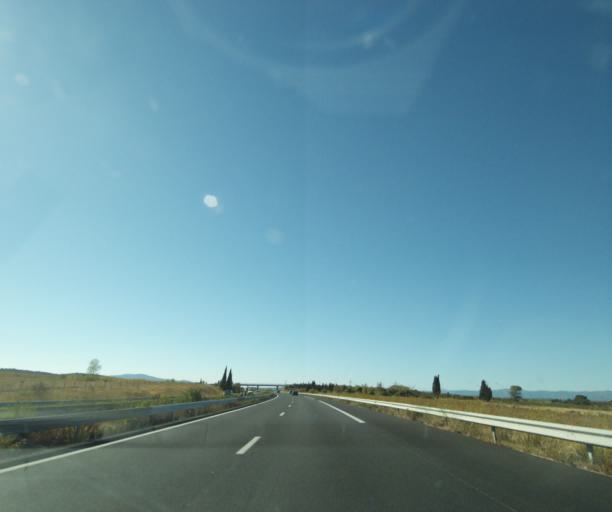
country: FR
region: Languedoc-Roussillon
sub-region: Departement de l'Aude
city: Ornaisons
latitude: 43.1672
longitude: 2.8364
